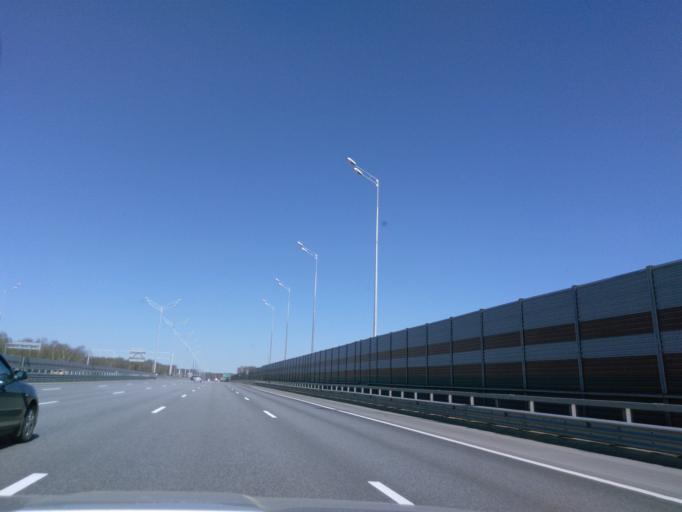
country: RU
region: Moskovskaya
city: Levoberezhnaya
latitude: 55.9089
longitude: 37.4736
